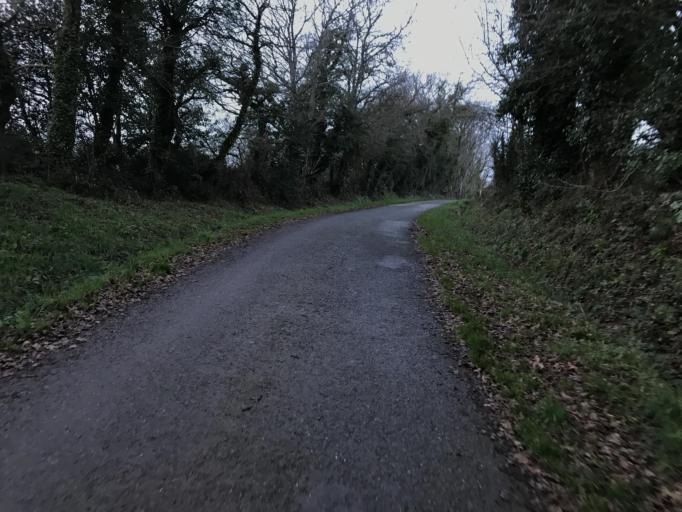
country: FR
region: Brittany
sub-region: Departement du Finistere
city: Loperhet
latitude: 48.3679
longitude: -4.3166
